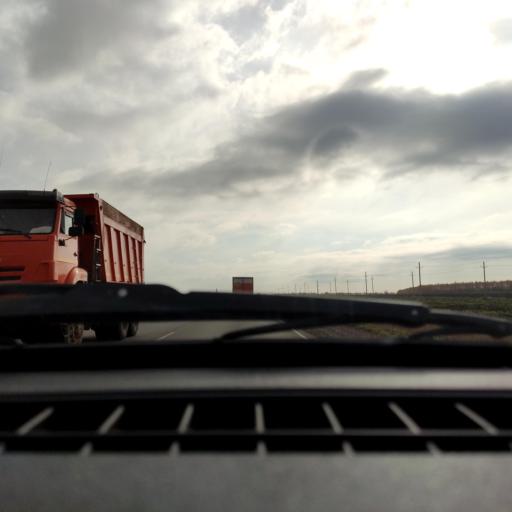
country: RU
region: Bashkortostan
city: Iglino
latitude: 54.7582
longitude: 56.2765
